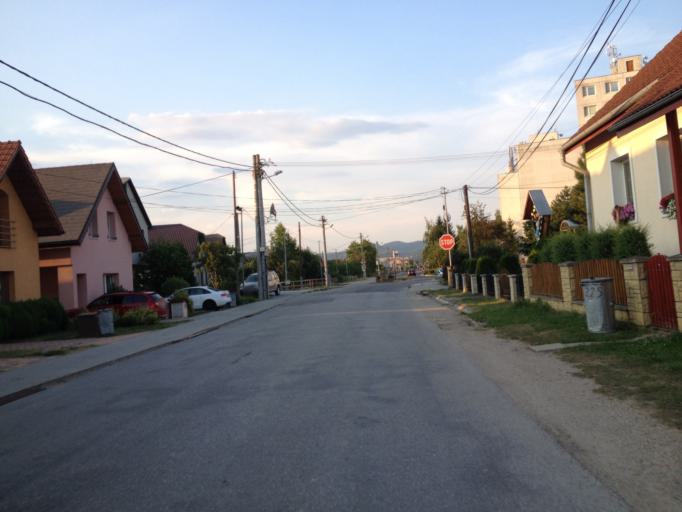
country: SK
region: Nitriansky
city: Puchov
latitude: 49.0601
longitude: 18.3218
